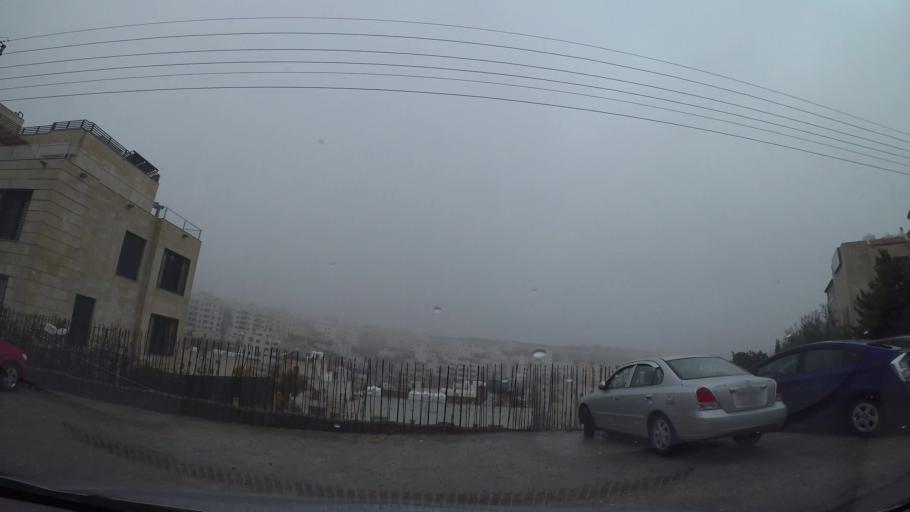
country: JO
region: Amman
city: Al Jubayhah
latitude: 32.0132
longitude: 35.8351
